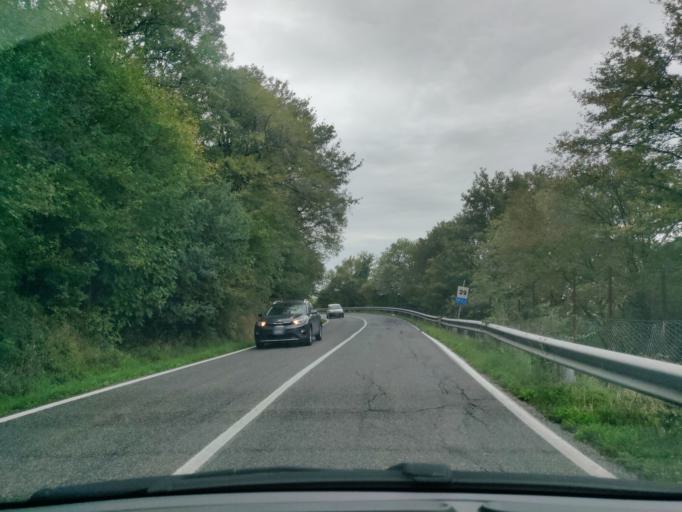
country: IT
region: Latium
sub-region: Citta metropolitana di Roma Capitale
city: Allumiere
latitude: 42.1451
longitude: 11.8907
